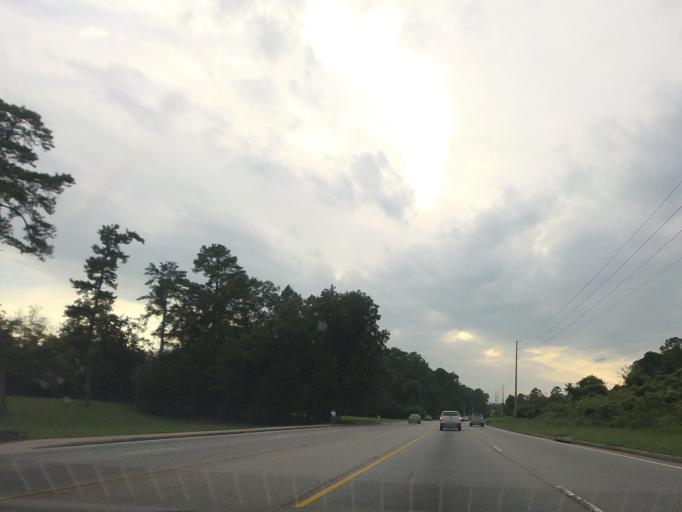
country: US
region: Georgia
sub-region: Bibb County
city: Macon
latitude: 32.8789
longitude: -83.7214
